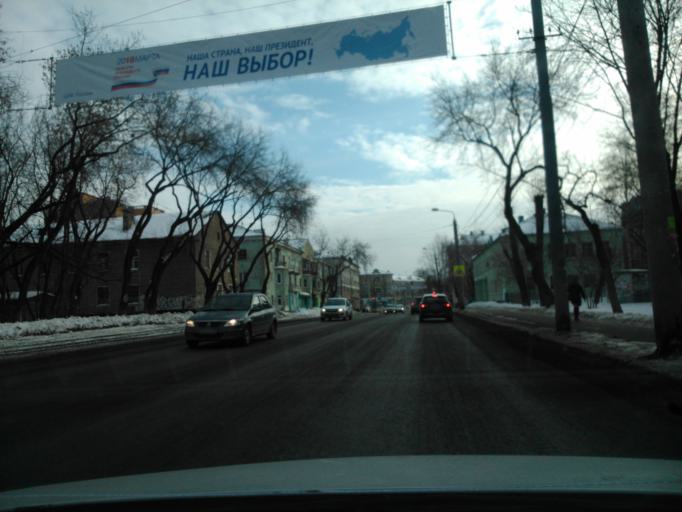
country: RU
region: Perm
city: Perm
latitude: 57.9955
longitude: 56.2459
